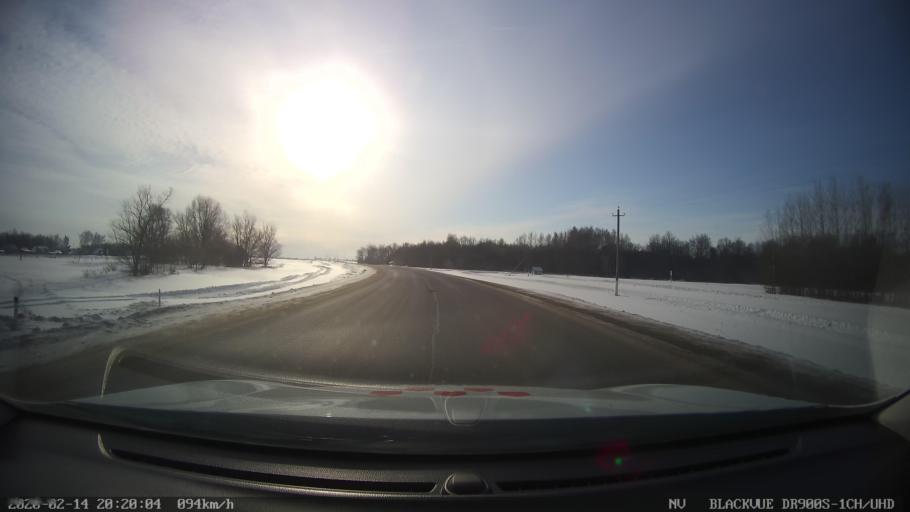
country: RU
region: Tatarstan
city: Verkhniy Uslon
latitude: 55.5613
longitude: 48.9017
